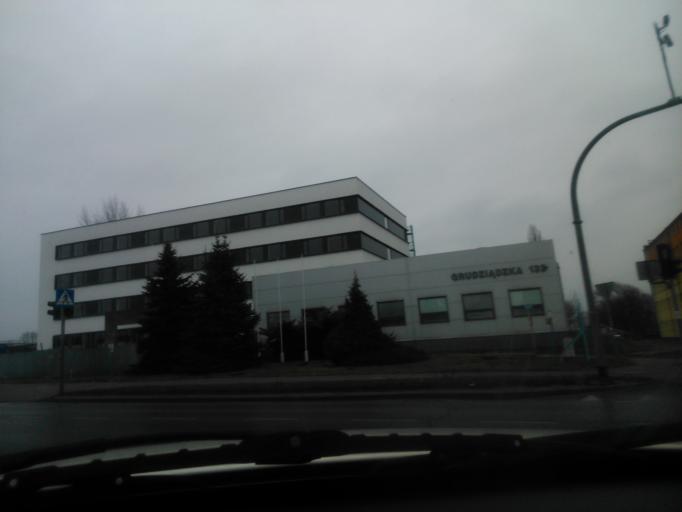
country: PL
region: Kujawsko-Pomorskie
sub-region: Torun
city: Torun
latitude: 53.0314
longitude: 18.6106
